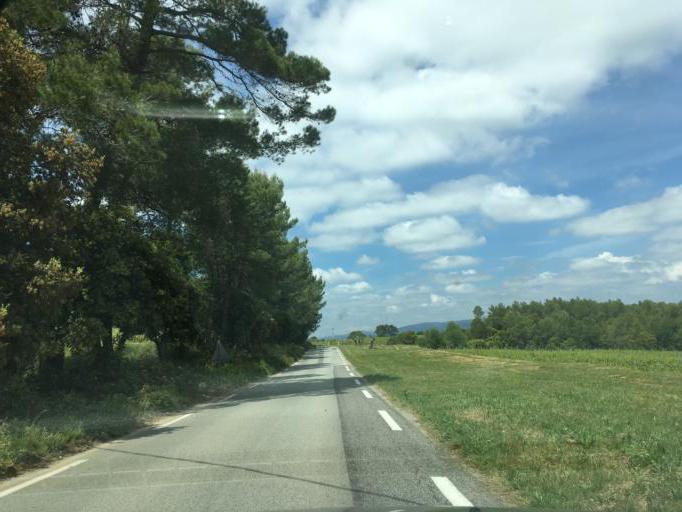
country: FR
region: Provence-Alpes-Cote d'Azur
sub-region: Departement du Var
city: Taradeau
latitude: 43.4766
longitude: 6.4319
